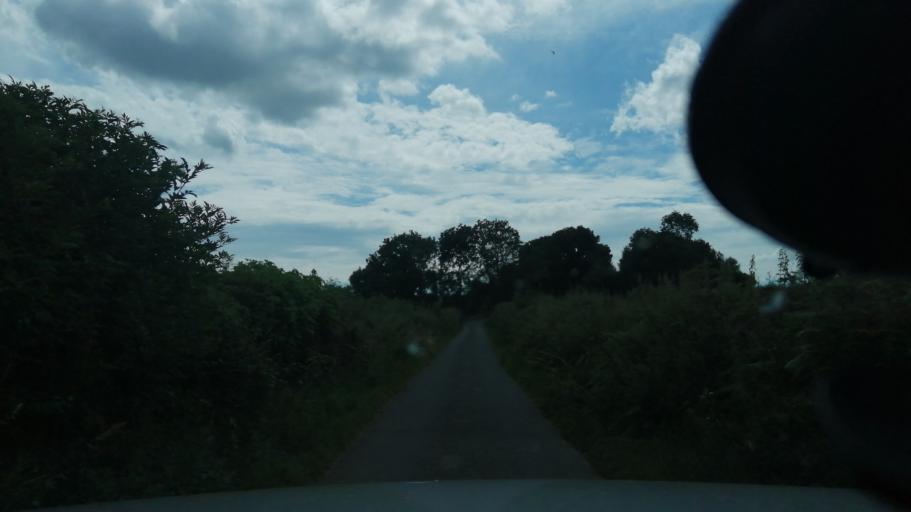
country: GB
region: England
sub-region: Herefordshire
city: Thruxton
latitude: 52.0141
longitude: -2.8068
